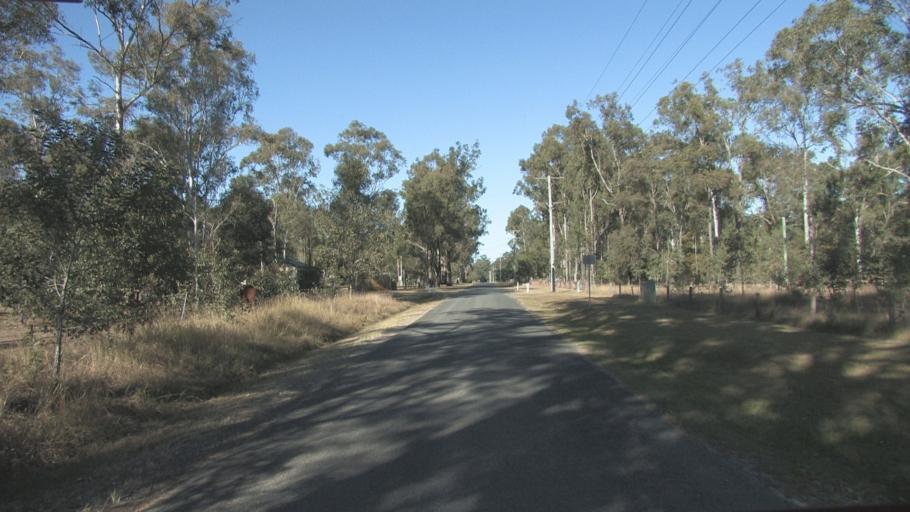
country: AU
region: Queensland
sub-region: Logan
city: North Maclean
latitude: -27.7529
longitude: 153.0342
